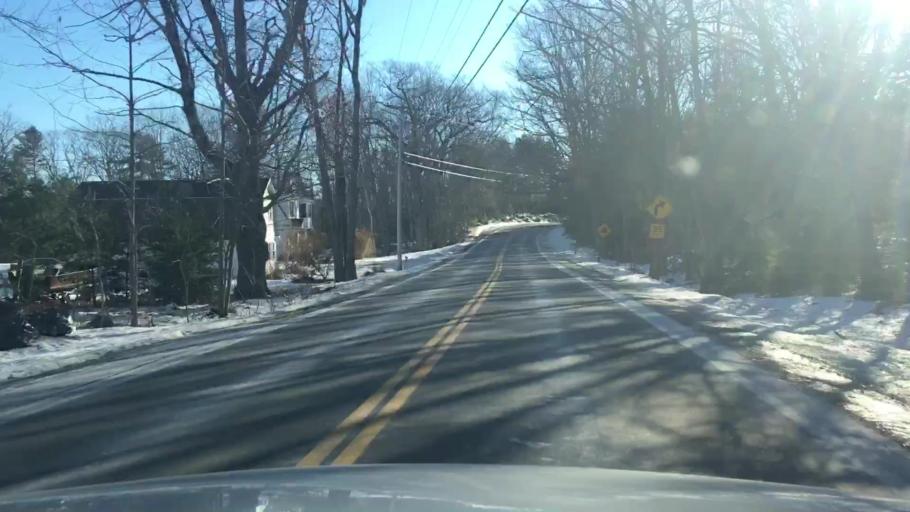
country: US
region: Maine
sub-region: Hancock County
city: Orland
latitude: 44.5133
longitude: -68.7528
